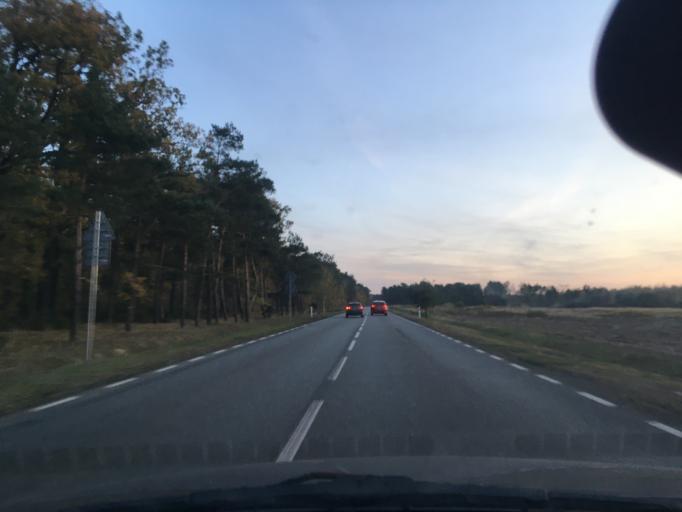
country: PL
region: Masovian Voivodeship
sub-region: Powiat sochaczewski
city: Mlodzieszyn
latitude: 52.3415
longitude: 20.2129
